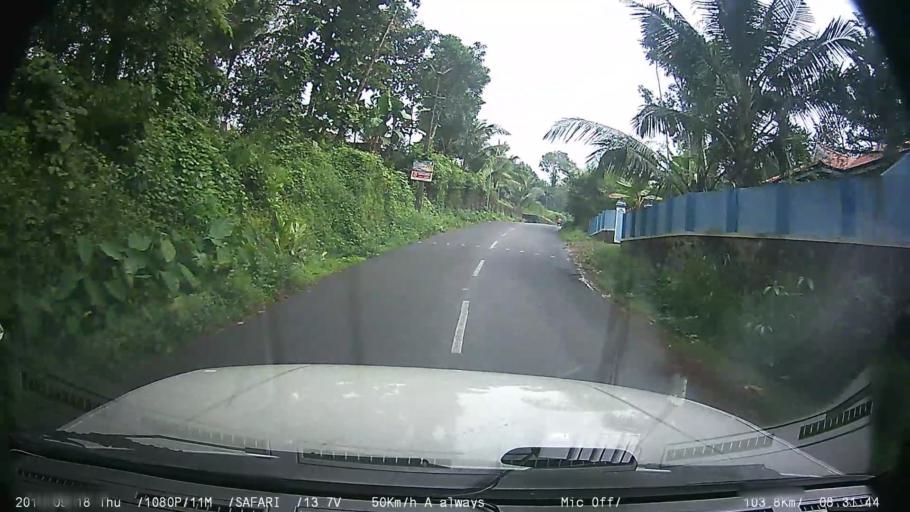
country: IN
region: Kerala
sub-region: Kottayam
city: Palackattumala
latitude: 9.7021
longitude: 76.6091
